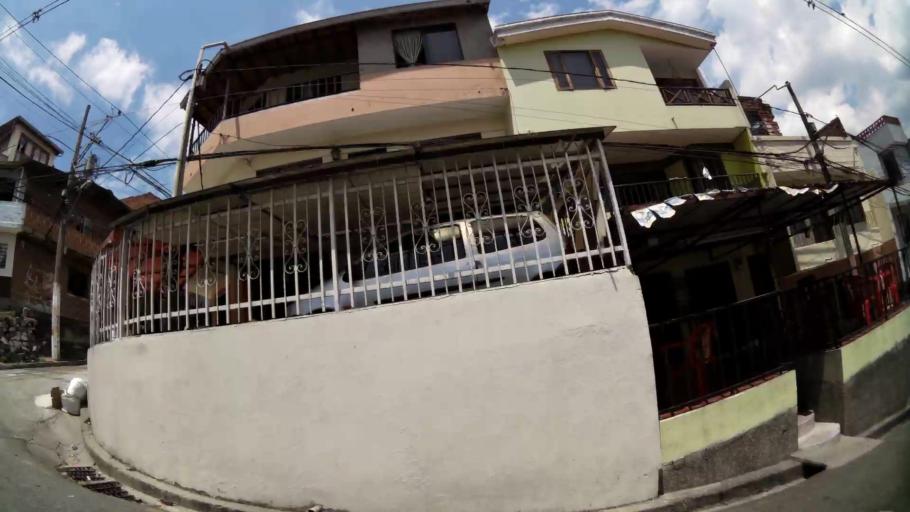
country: CO
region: Antioquia
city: Bello
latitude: 6.2957
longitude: -75.5769
